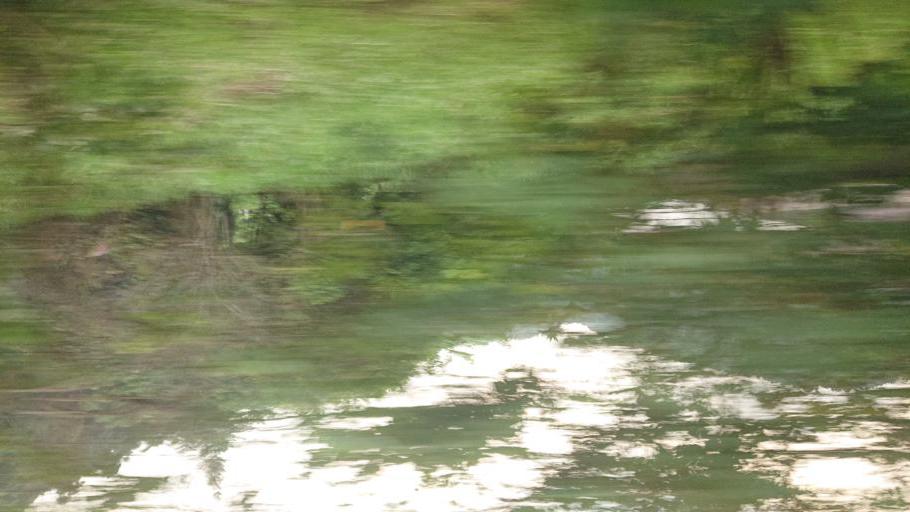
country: TW
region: Taiwan
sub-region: Nantou
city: Puli
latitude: 23.9701
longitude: 120.9971
